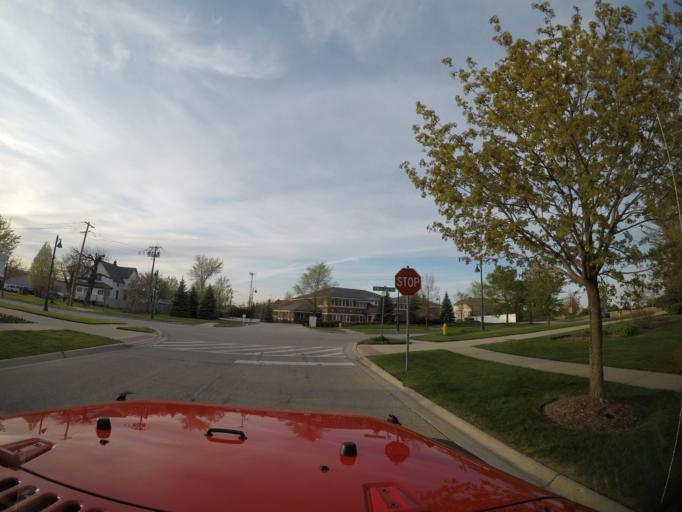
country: US
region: Illinois
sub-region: Cook County
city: Northbrook
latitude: 42.0873
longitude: -87.8343
